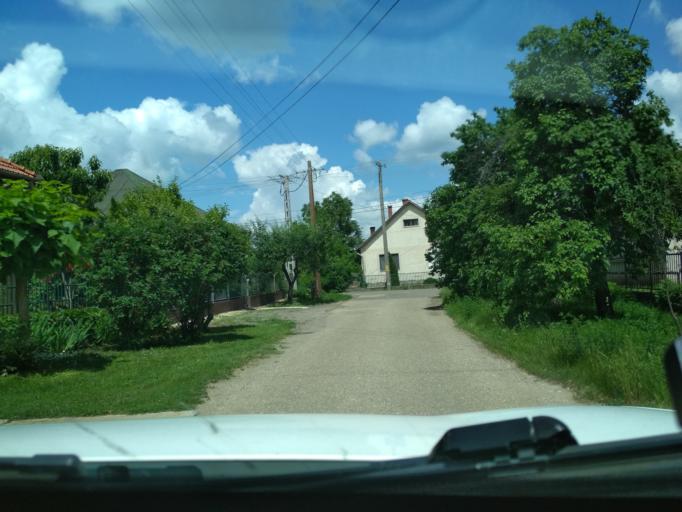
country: HU
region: Jasz-Nagykun-Szolnok
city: Tiszafured
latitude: 47.6085
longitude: 20.7728
